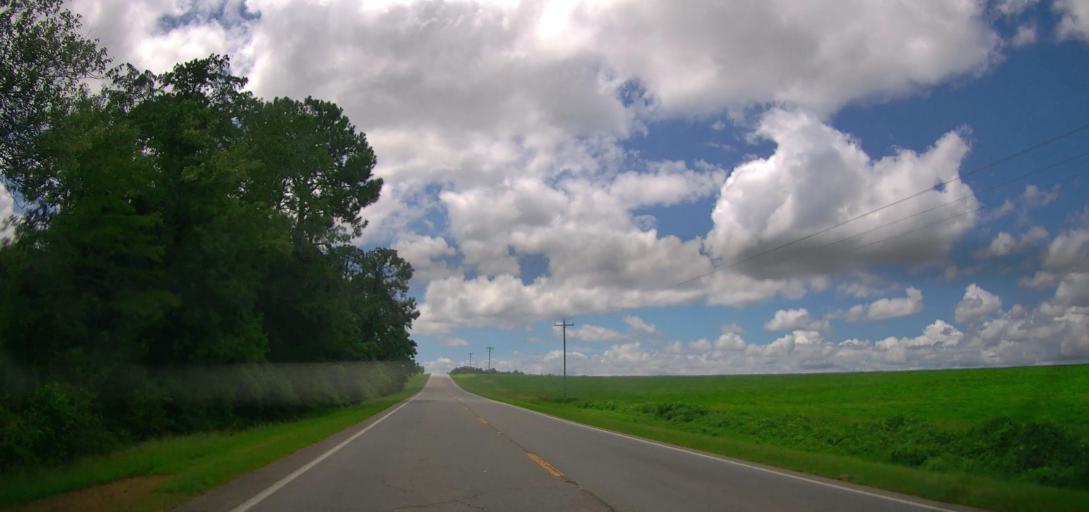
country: US
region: Georgia
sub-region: Turner County
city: Ashburn
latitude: 31.7216
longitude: -83.5117
